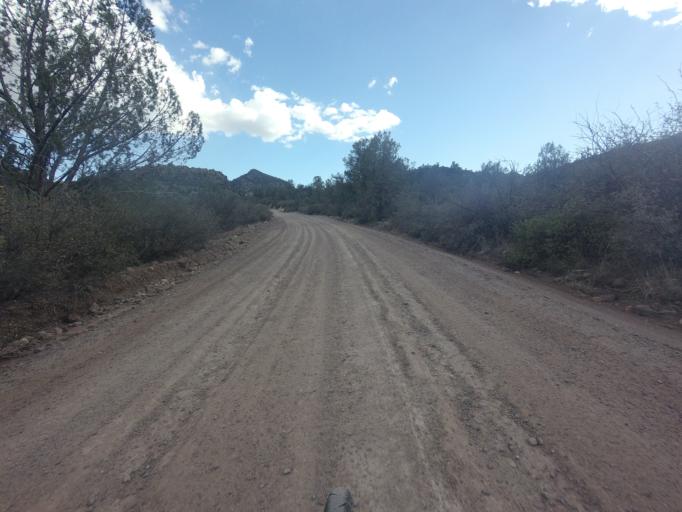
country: US
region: Arizona
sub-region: Yavapai County
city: Camp Verde
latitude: 34.4419
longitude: -111.6884
